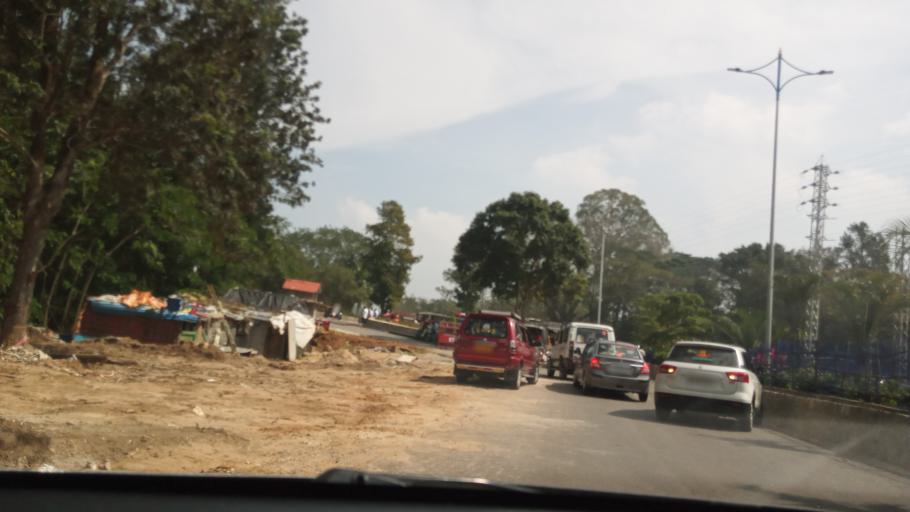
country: IN
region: Andhra Pradesh
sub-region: Chittoor
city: Tirumala
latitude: 13.6898
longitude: 79.3512
